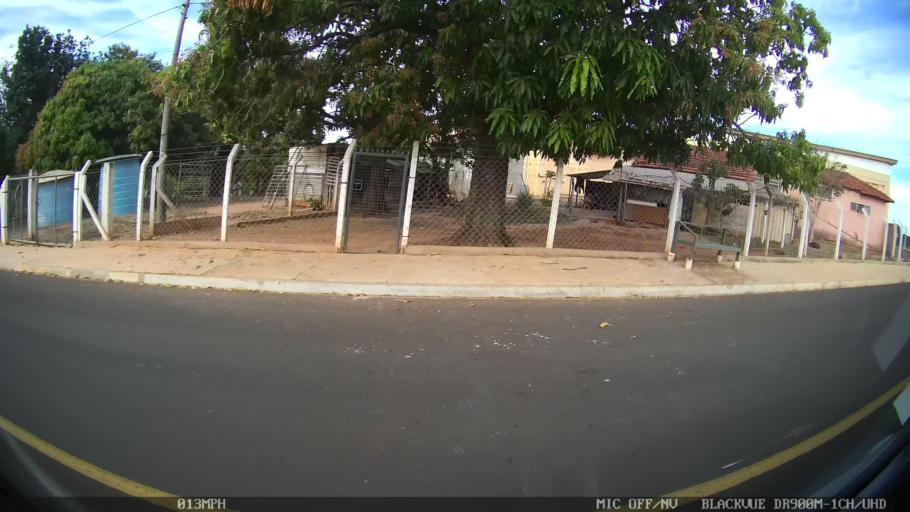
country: BR
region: Sao Paulo
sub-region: Catanduva
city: Catanduva
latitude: -21.1410
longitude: -49.0066
